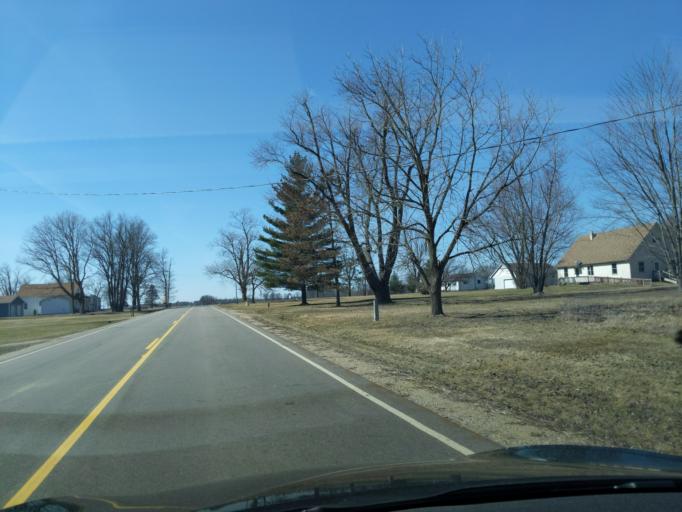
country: US
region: Michigan
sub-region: Ionia County
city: Lake Odessa
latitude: 42.7268
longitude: -85.0013
